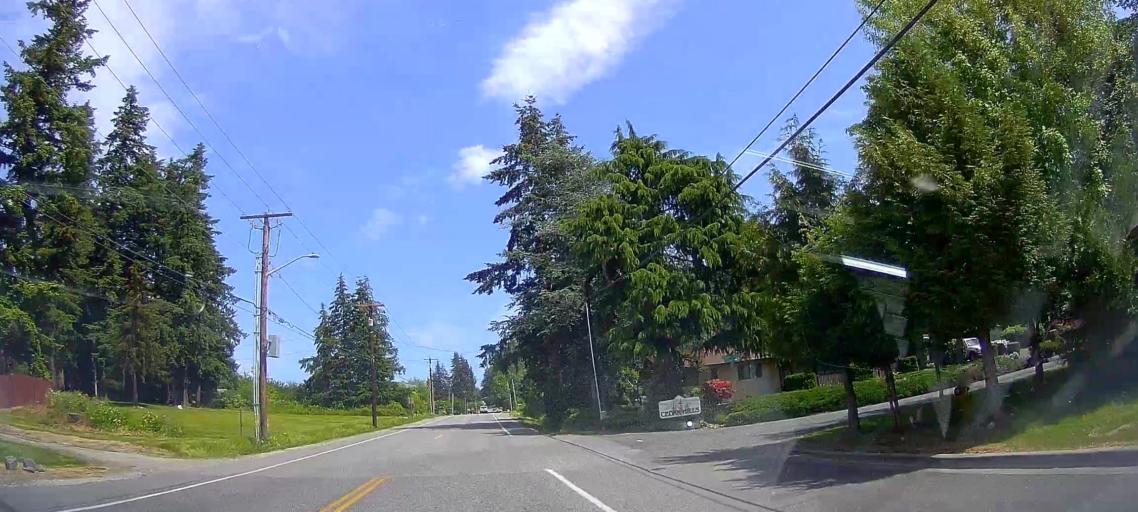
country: US
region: Washington
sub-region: Skagit County
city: Mount Vernon
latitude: 48.4065
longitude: -122.3114
